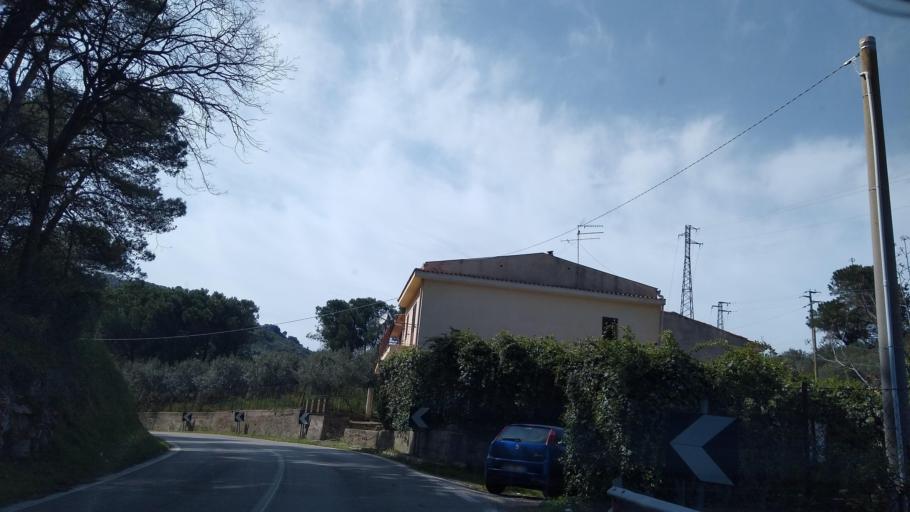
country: IT
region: Sicily
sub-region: Palermo
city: Pioppo
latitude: 38.0414
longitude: 13.2022
